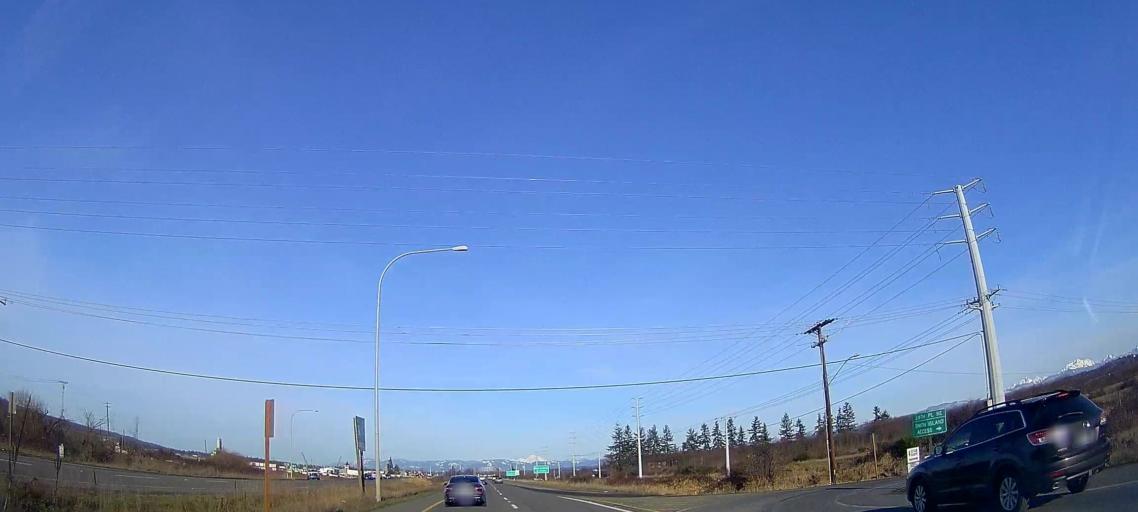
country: US
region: Washington
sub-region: Snohomish County
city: Marysville
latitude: 48.0240
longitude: -122.1850
